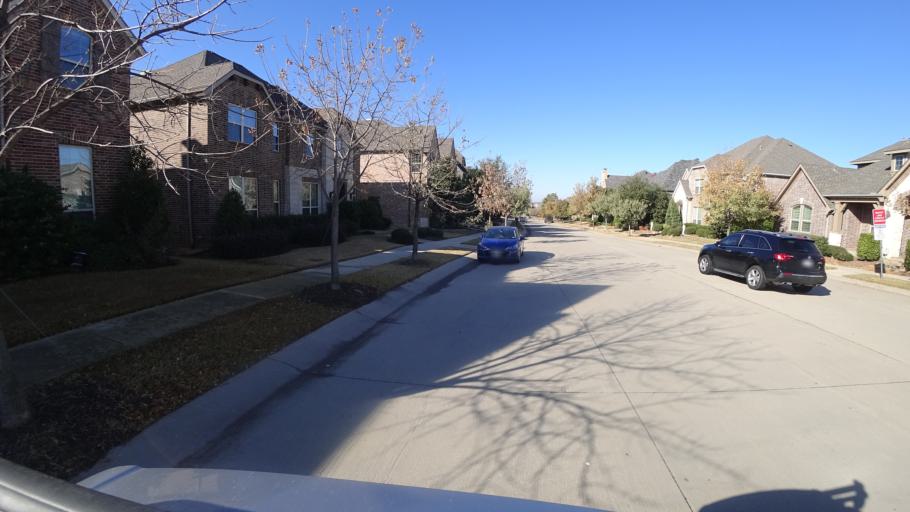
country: US
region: Texas
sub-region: Denton County
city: The Colony
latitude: 33.0395
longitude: -96.9188
